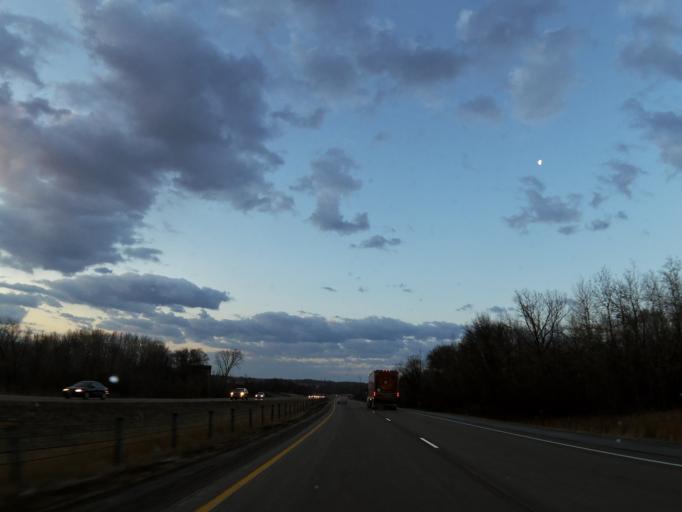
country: US
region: Minnesota
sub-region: Scott County
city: Elko New Market
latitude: 44.6183
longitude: -93.2981
